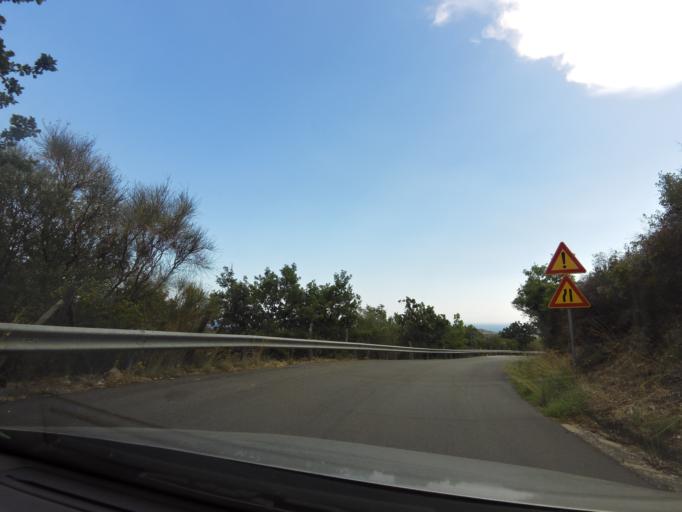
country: IT
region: Calabria
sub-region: Provincia di Reggio Calabria
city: Camini
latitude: 38.4367
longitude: 16.5144
